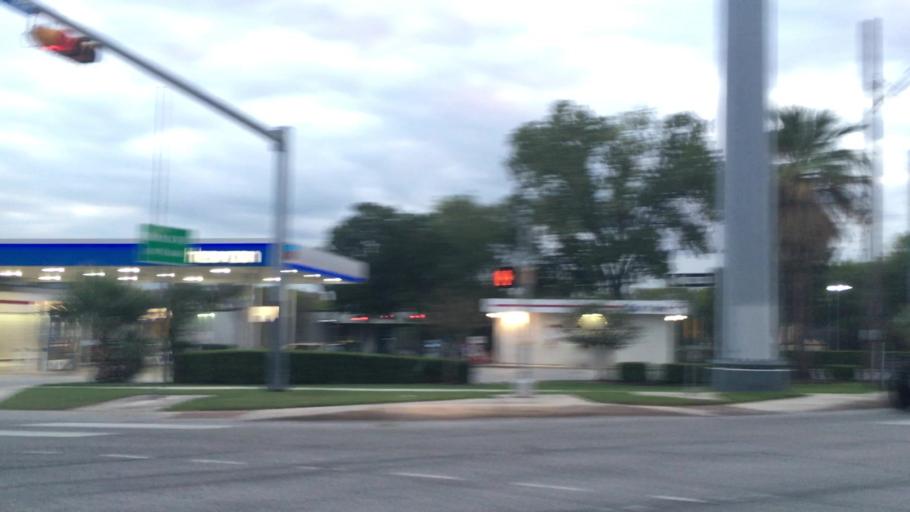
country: US
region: Texas
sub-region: Bexar County
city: Balcones Heights
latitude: 29.4893
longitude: -98.5744
